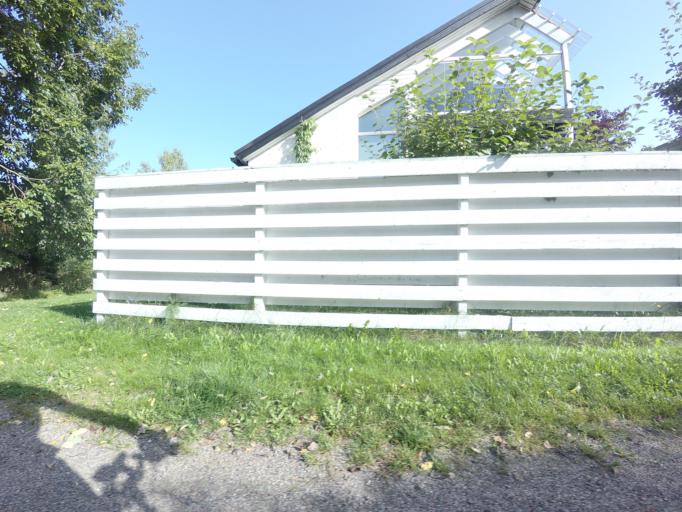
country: FI
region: Uusimaa
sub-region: Helsinki
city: Espoo
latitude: 60.1759
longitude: 24.6587
